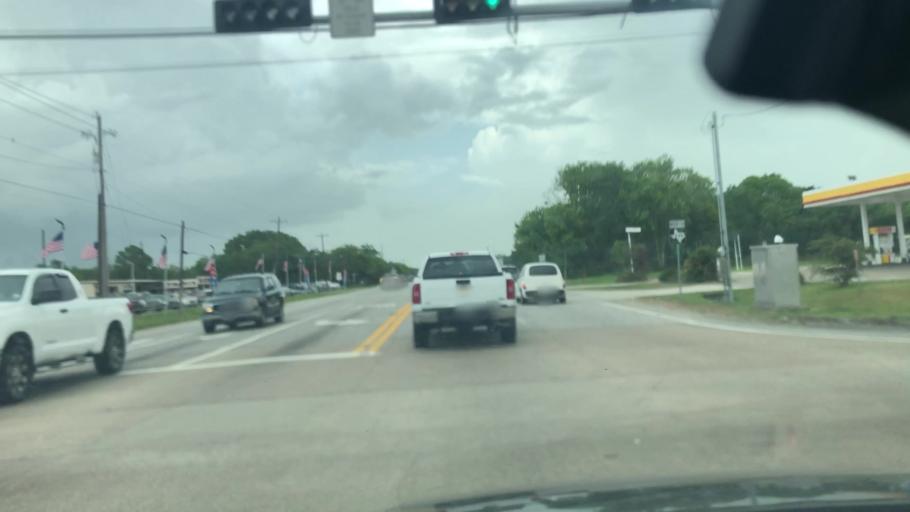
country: US
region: Texas
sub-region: Galveston County
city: Dickinson
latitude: 29.4804
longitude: -95.0698
